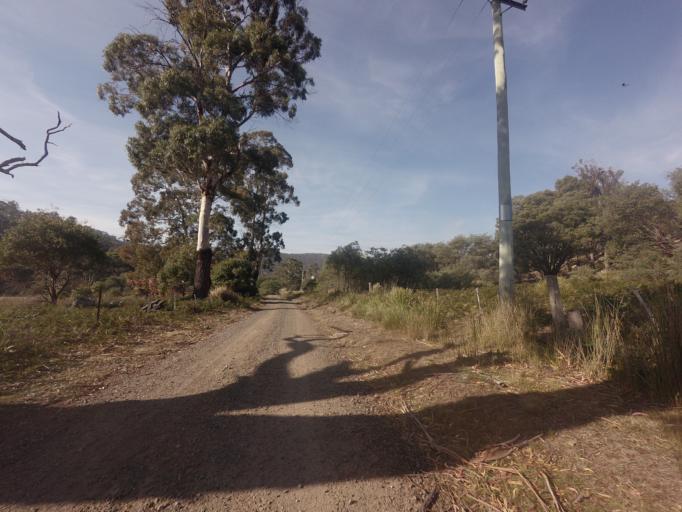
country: AU
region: Tasmania
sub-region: Sorell
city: Sorell
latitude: -42.5320
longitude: 147.4385
